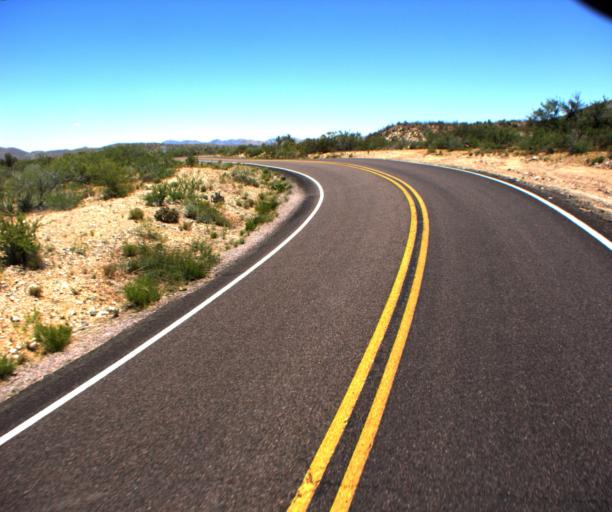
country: US
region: Arizona
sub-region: Yavapai County
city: Bagdad
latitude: 34.4849
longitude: -113.1838
